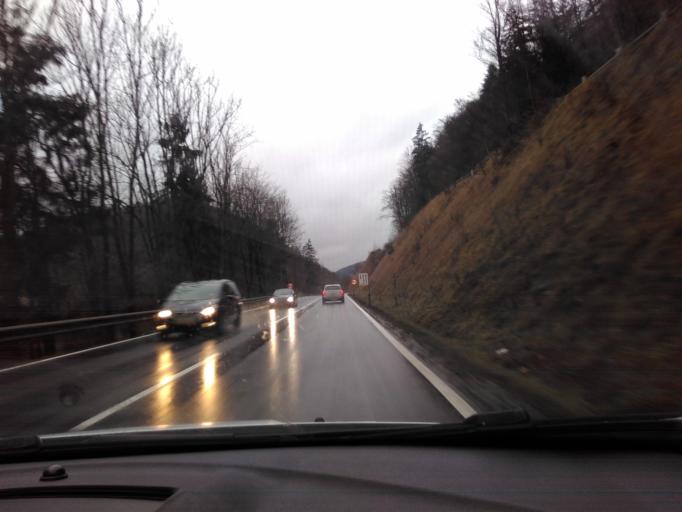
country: AT
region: Upper Austria
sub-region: Politischer Bezirk Urfahr-Umgebung
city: Kirchschlag bei Linz
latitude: 48.3795
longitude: 14.2926
